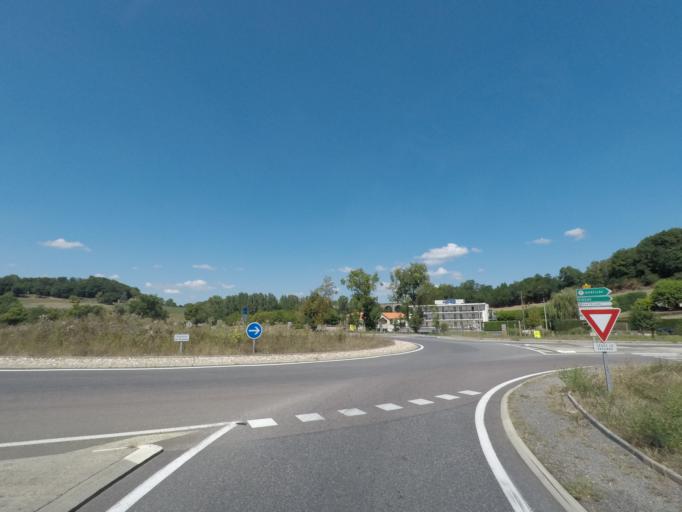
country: FR
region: Midi-Pyrenees
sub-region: Departement du Lot
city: Figeac
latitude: 44.5956
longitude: 1.9754
